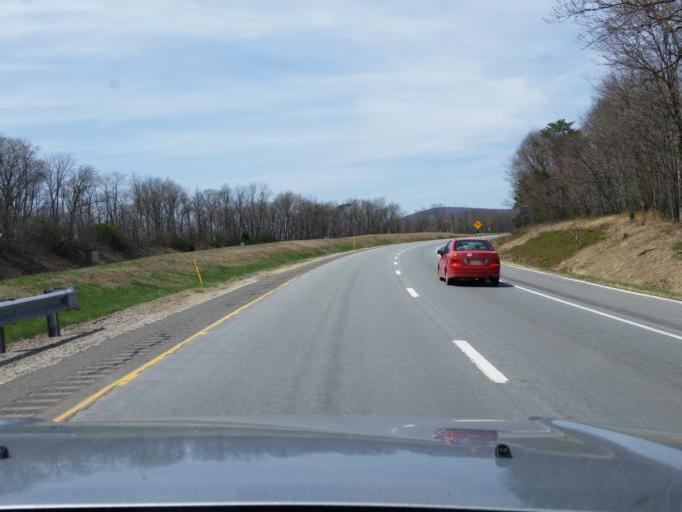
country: US
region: Pennsylvania
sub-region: Perry County
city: Newport
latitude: 40.4790
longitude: -77.0686
